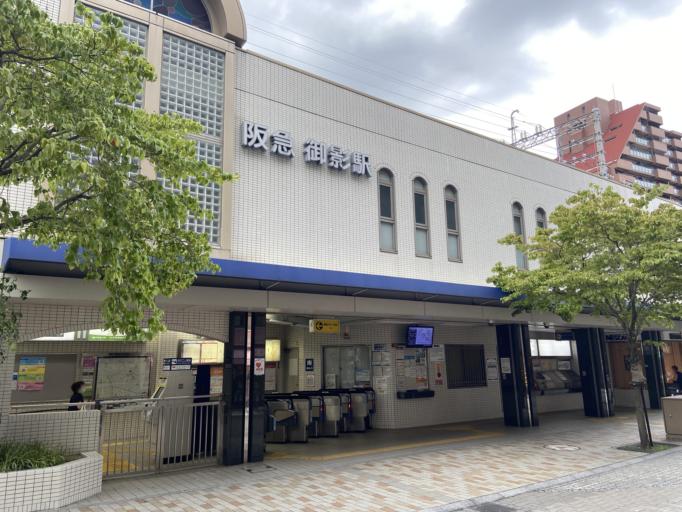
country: JP
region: Hyogo
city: Ashiya
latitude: 34.7245
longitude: 135.2528
